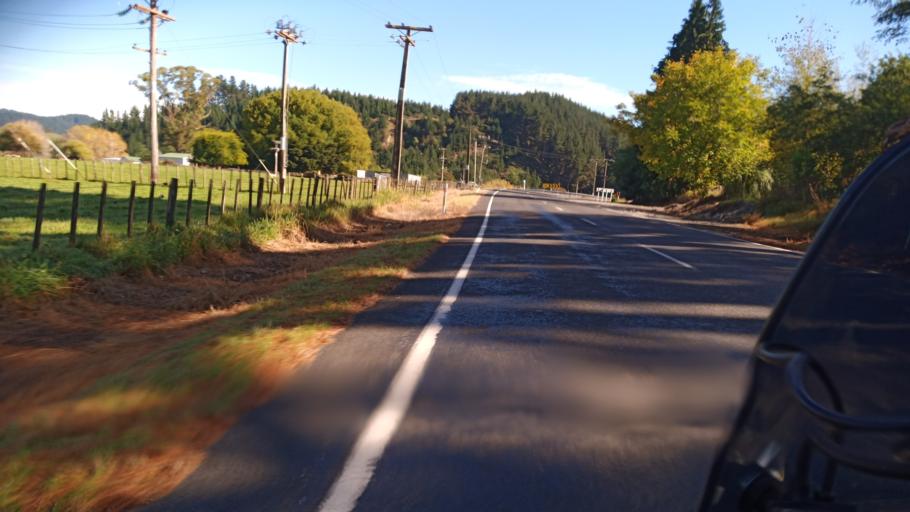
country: NZ
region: Hawke's Bay
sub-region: Wairoa District
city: Wairoa
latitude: -38.9220
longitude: 177.2677
